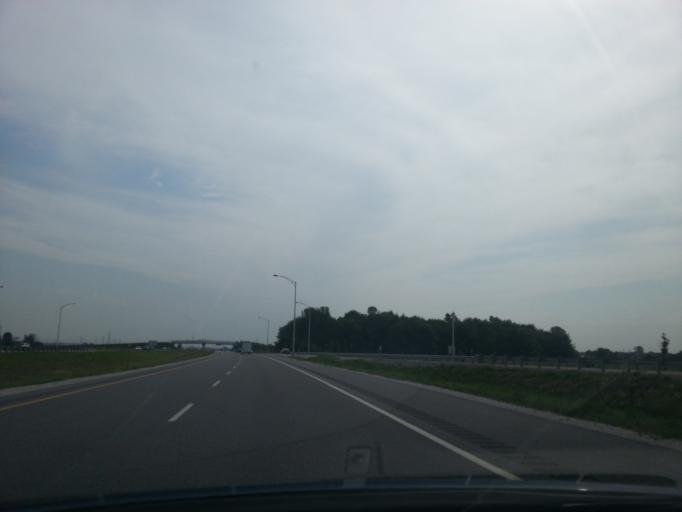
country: CA
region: Quebec
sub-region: Monteregie
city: Beauharnois
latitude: 45.3051
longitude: -73.8596
